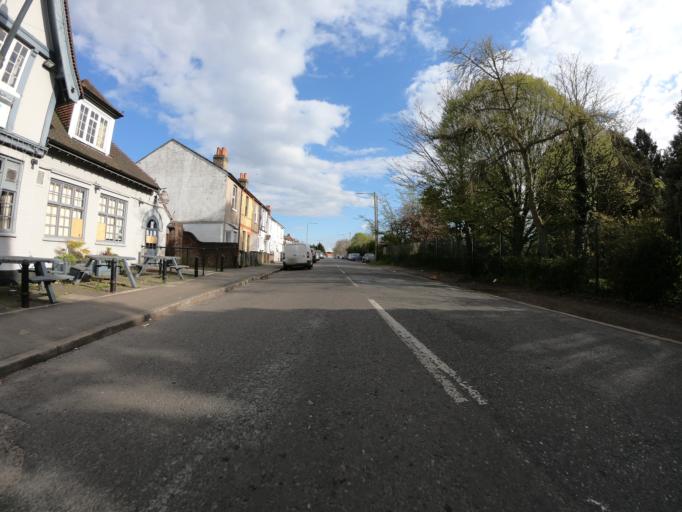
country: GB
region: England
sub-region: Greater London
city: Bexleyheath
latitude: 51.4634
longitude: 0.1509
